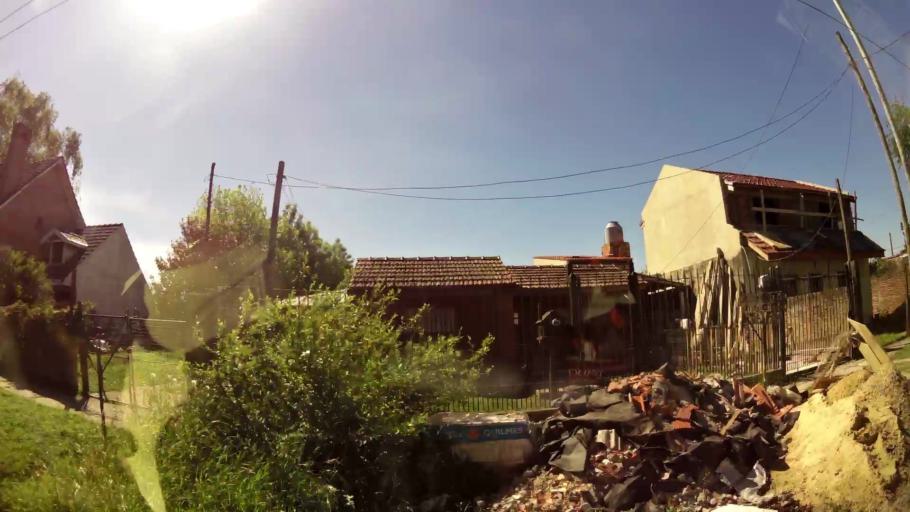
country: AR
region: Buenos Aires
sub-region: Partido de Almirante Brown
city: Adrogue
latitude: -34.7992
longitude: -58.3622
